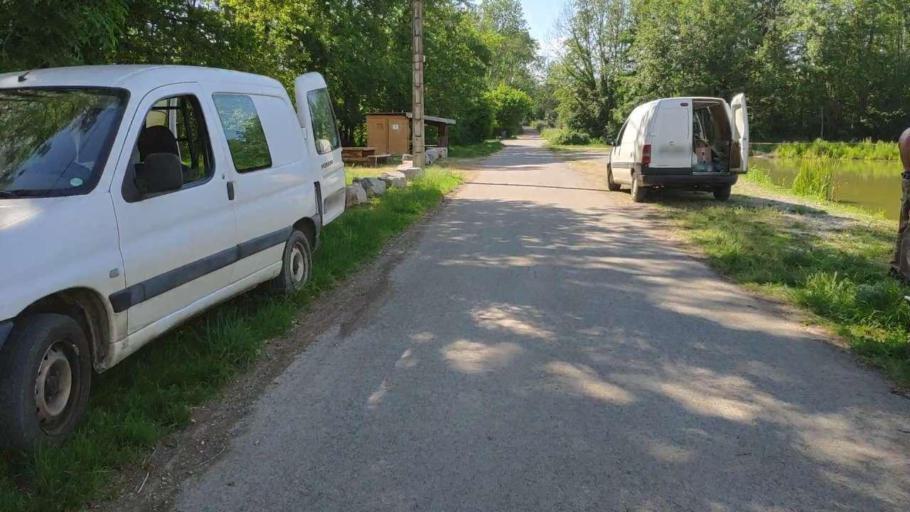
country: FR
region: Franche-Comte
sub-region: Departement du Jura
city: Bletterans
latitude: 46.7662
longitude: 5.4604
